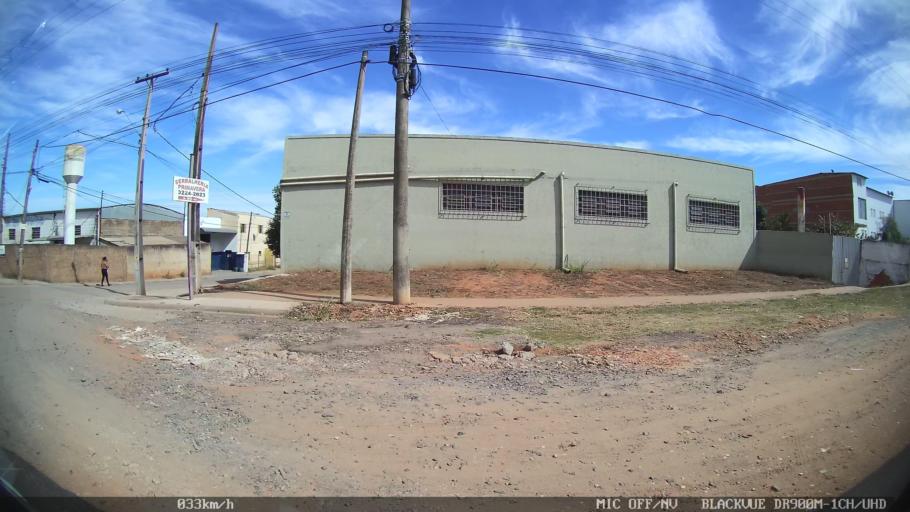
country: BR
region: Sao Paulo
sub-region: Sao Jose Do Rio Preto
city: Sao Jose do Rio Preto
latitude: -20.8367
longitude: -49.3362
